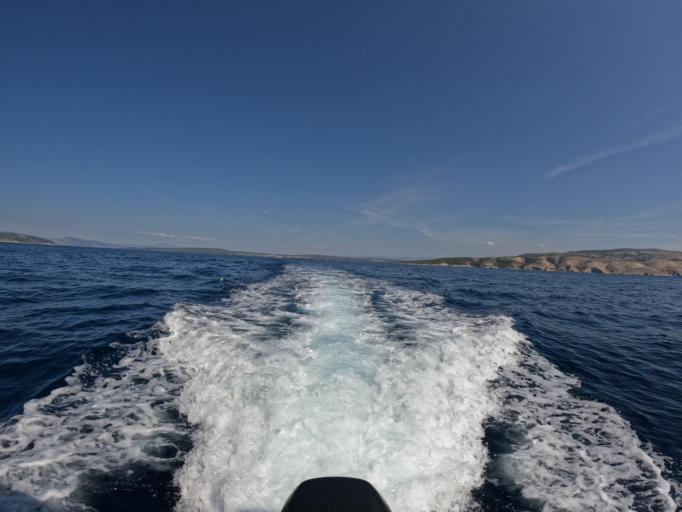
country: HR
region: Primorsko-Goranska
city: Punat
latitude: 44.9487
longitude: 14.6130
